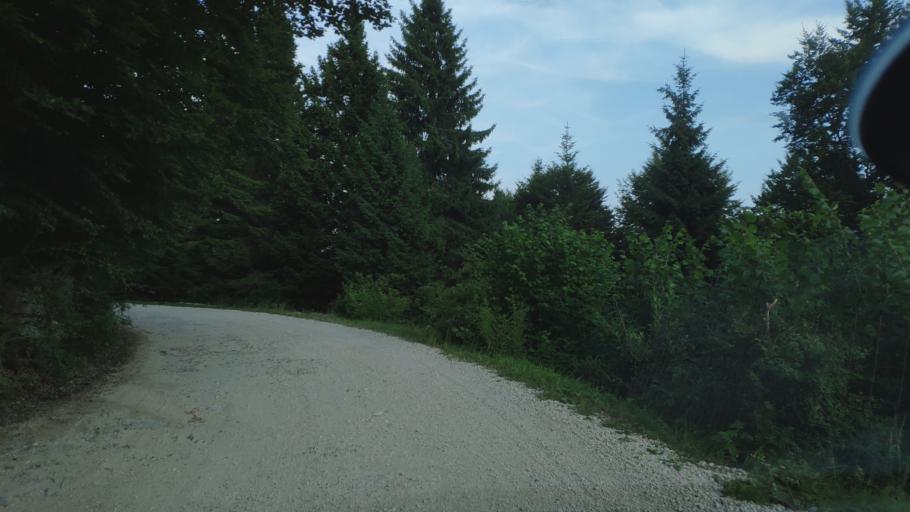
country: IT
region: Veneto
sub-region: Provincia di Vicenza
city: Calvene
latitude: 45.8011
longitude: 11.5052
